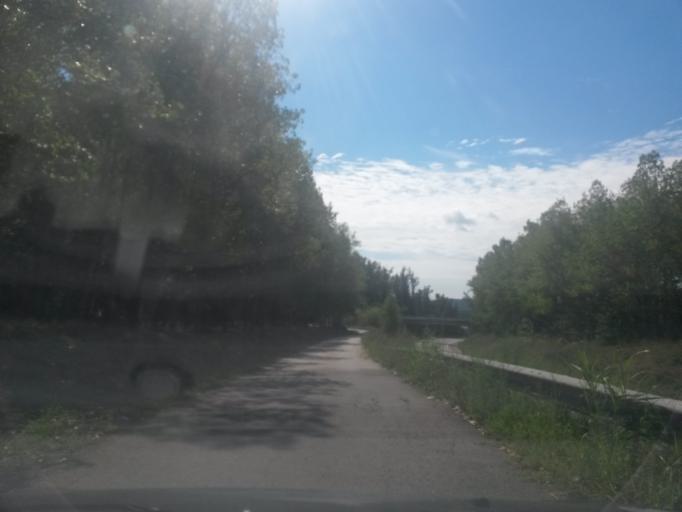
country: ES
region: Catalonia
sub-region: Provincia de Girona
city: la Cellera de Ter
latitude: 41.9779
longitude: 2.6210
